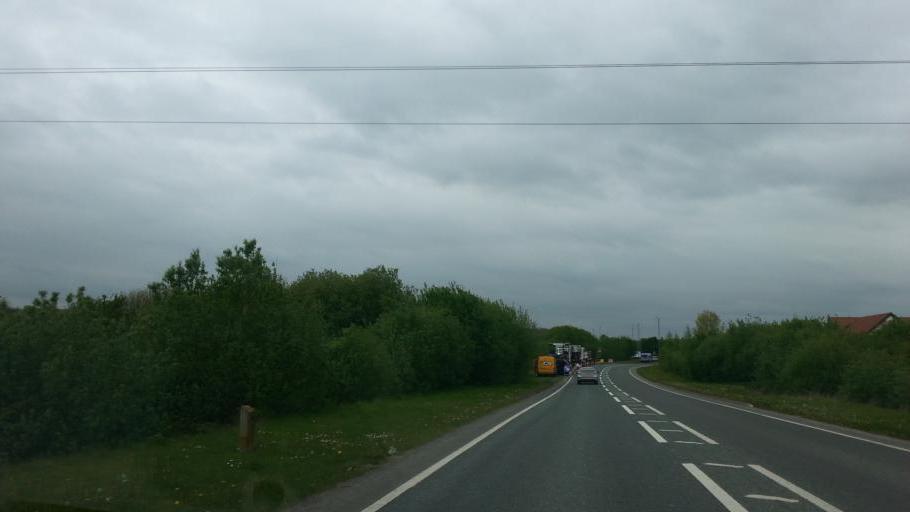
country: GB
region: England
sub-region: Lincolnshire
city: Bourne
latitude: 52.7634
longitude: -0.3957
